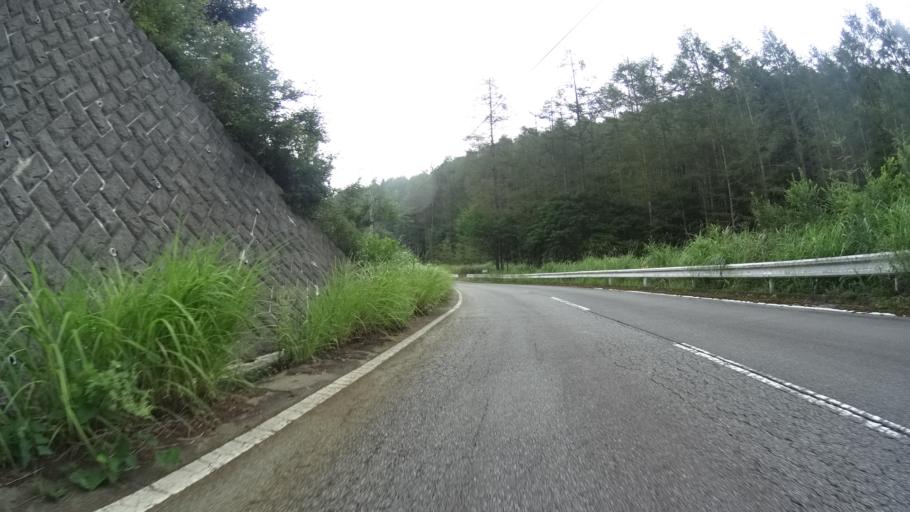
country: JP
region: Yamanashi
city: Enzan
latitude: 35.8068
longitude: 138.6521
